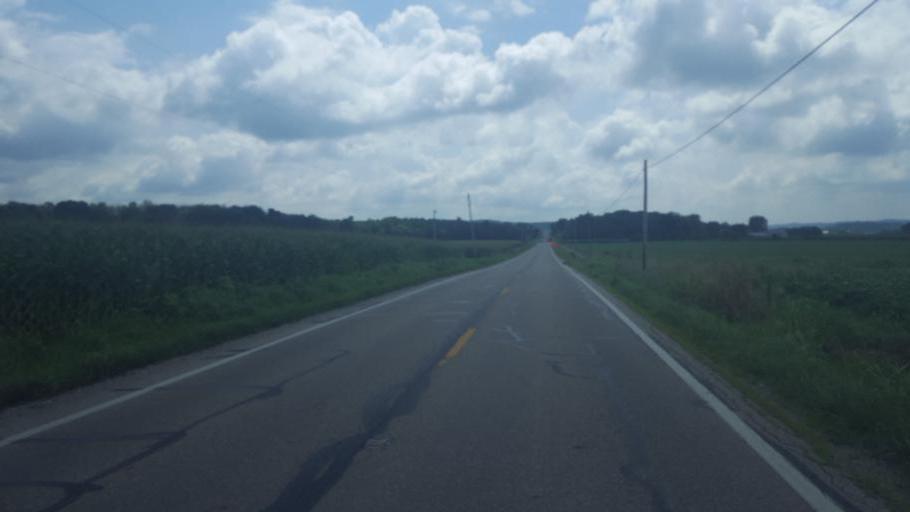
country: US
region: Ohio
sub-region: Ross County
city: Kingston
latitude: 39.4988
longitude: -82.7701
